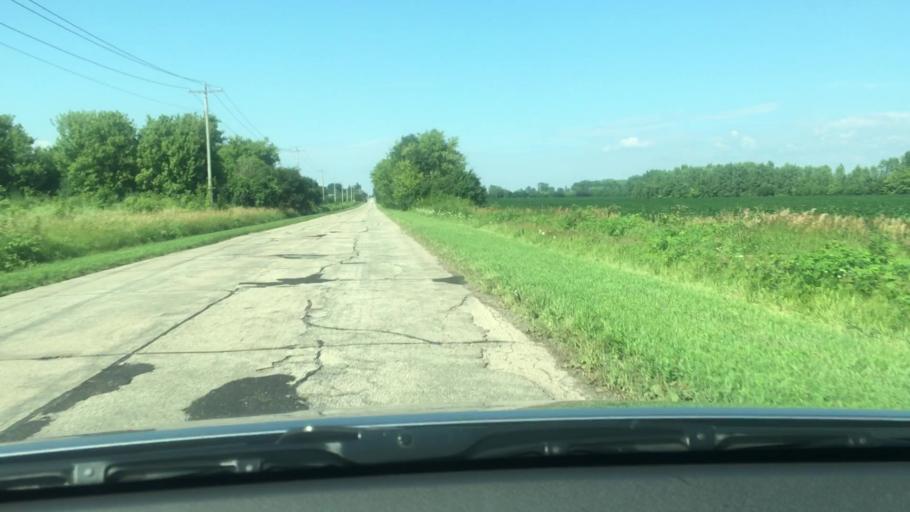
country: US
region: Wisconsin
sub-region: Winnebago County
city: Oshkosh
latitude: 43.9600
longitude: -88.5741
